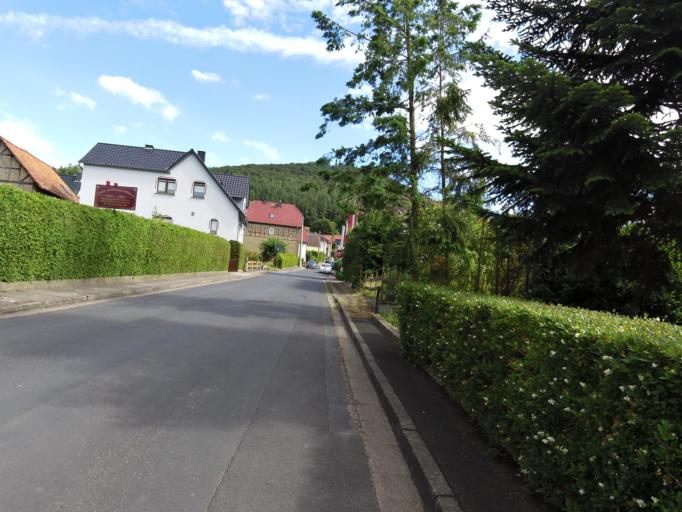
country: DE
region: Thuringia
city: Dorndorf
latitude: 50.8428
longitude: 10.1248
